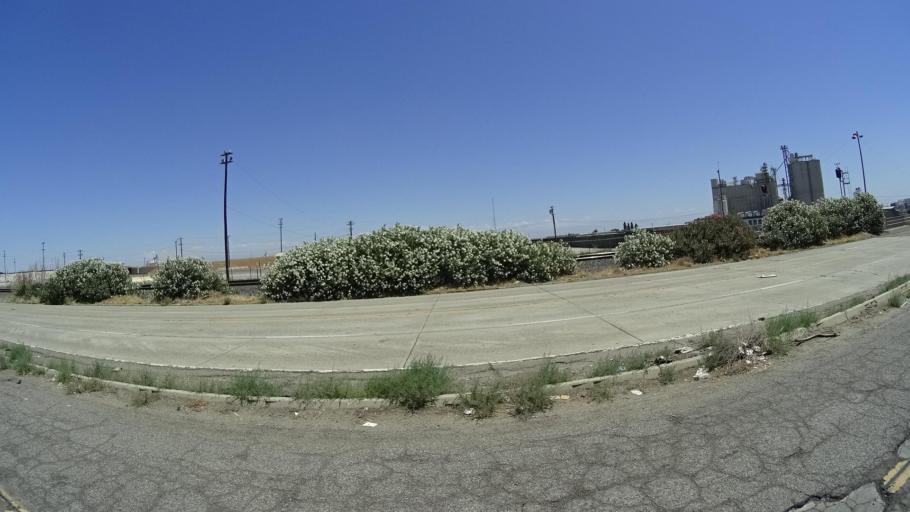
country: US
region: California
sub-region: Fresno County
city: Fresno
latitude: 36.6944
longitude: -119.7526
